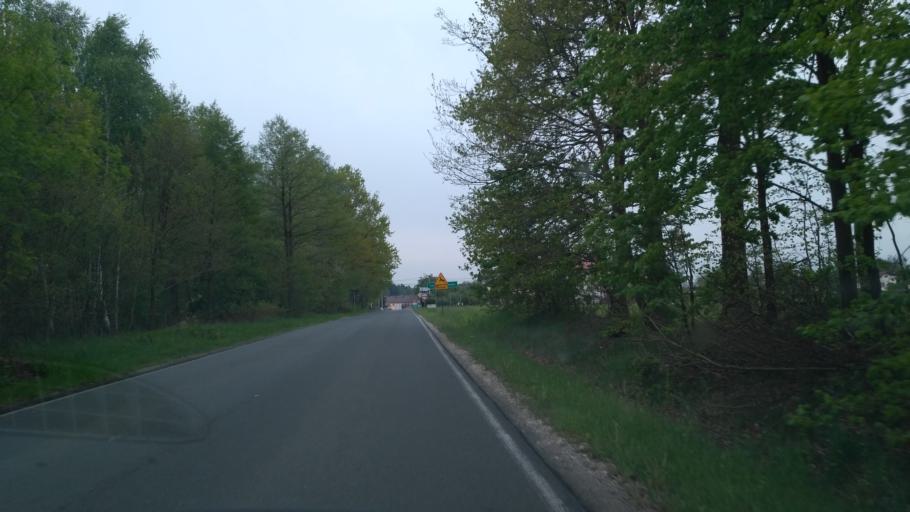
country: PL
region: Subcarpathian Voivodeship
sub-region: Powiat ropczycko-sedziszowski
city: Sedziszow Malopolski
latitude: 50.1280
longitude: 21.7540
